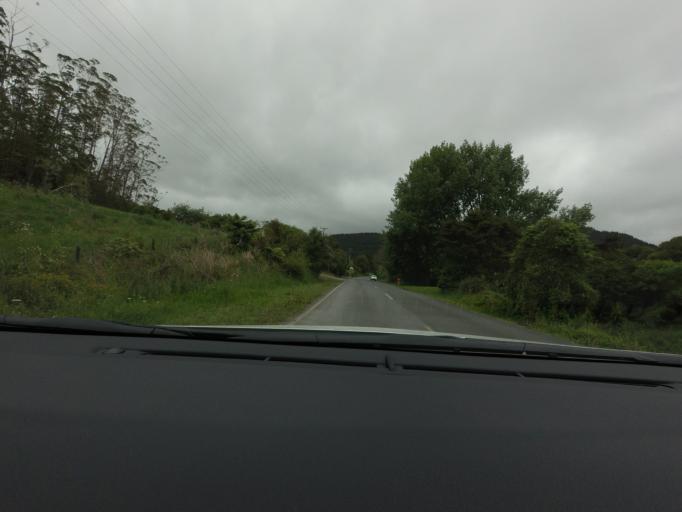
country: NZ
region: Auckland
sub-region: Auckland
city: Warkworth
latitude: -36.4742
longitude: 174.5543
